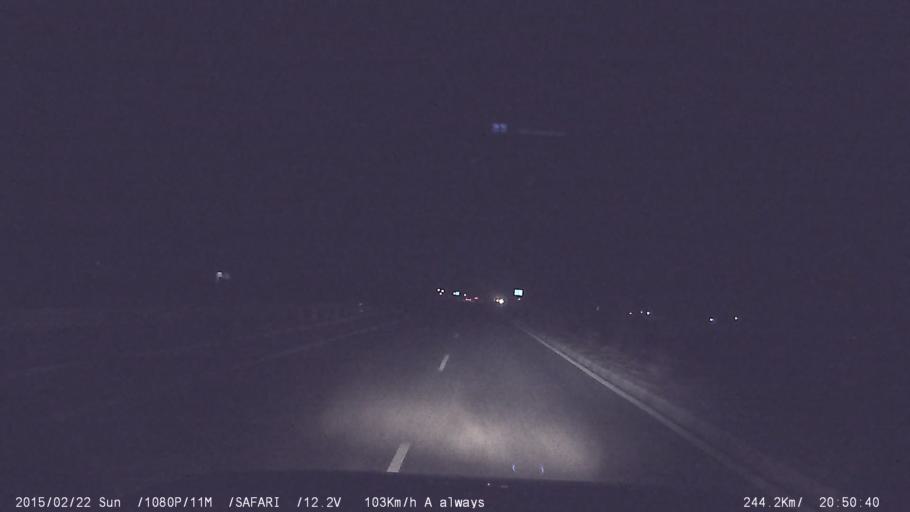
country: IN
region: Tamil Nadu
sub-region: Dindigul
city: Vedasandur
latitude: 10.5347
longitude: 77.9370
